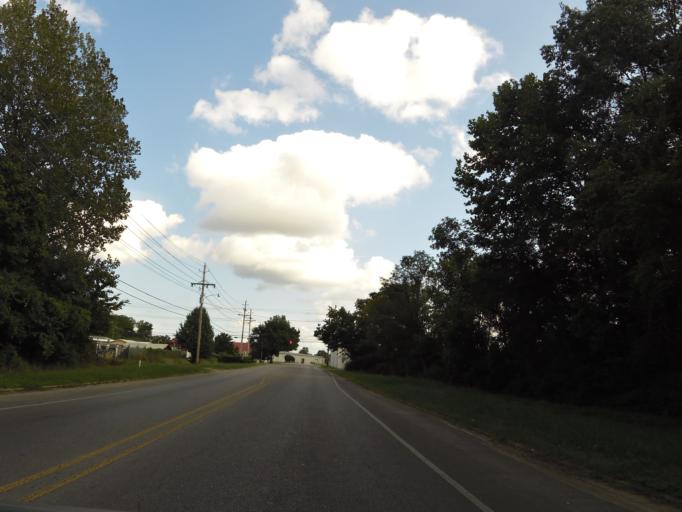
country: US
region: Mississippi
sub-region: Alcorn County
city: Corinth
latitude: 34.9314
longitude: -88.5266
